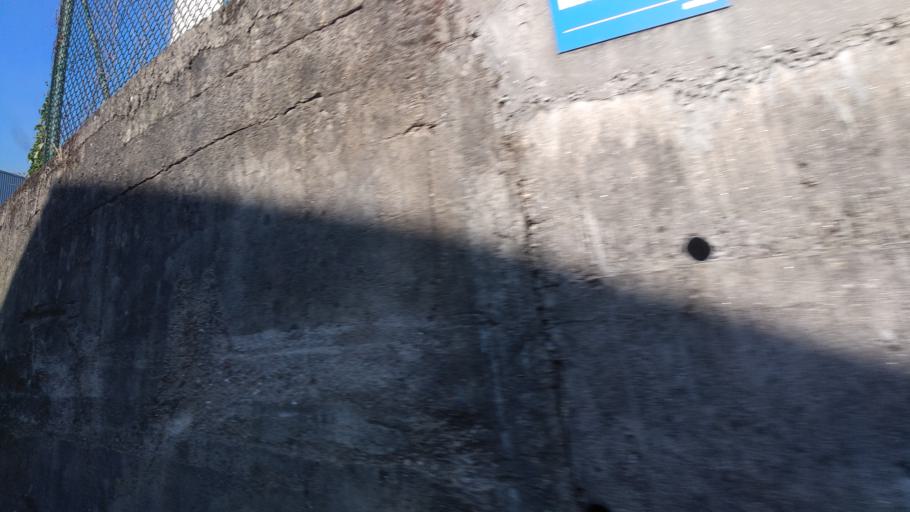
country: PT
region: Braga
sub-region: Braga
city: Braga
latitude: 41.5318
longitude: -8.4240
